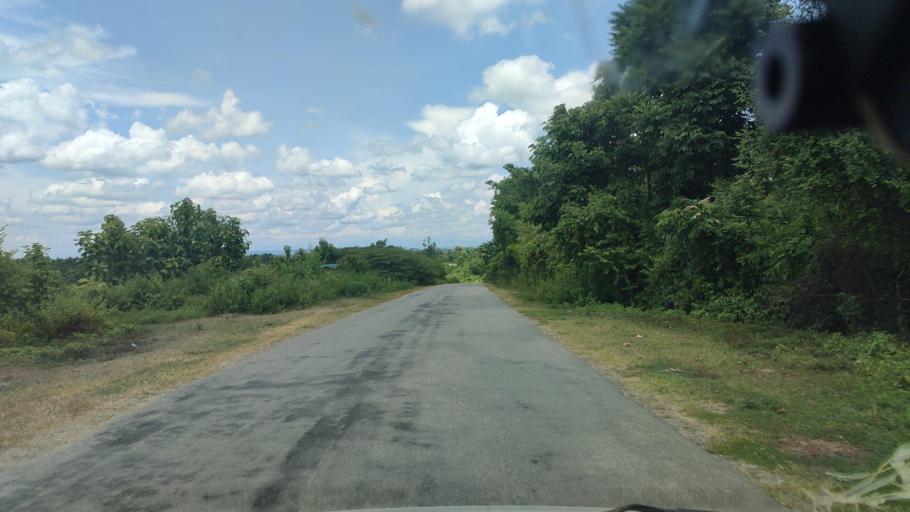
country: MM
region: Magway
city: Taungdwingyi
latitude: 19.9974
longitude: 95.8775
